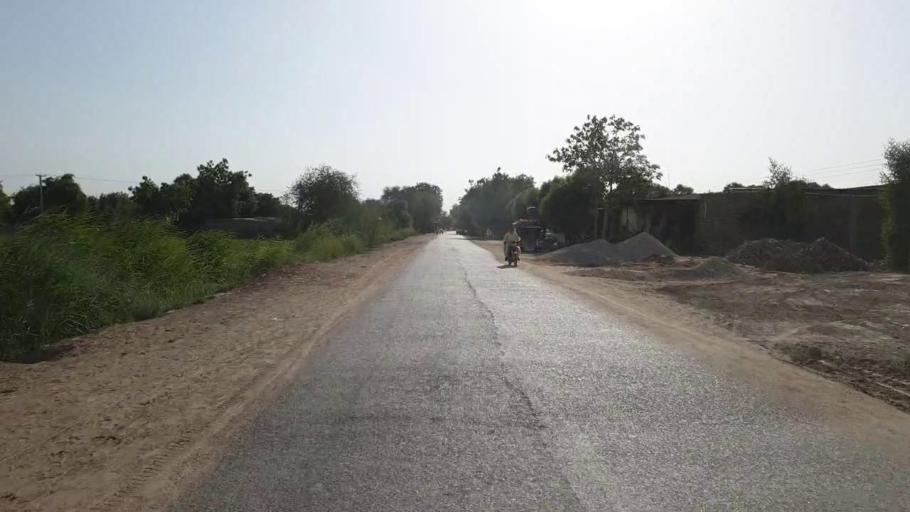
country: PK
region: Sindh
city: Daur
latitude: 26.4753
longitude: 68.4722
